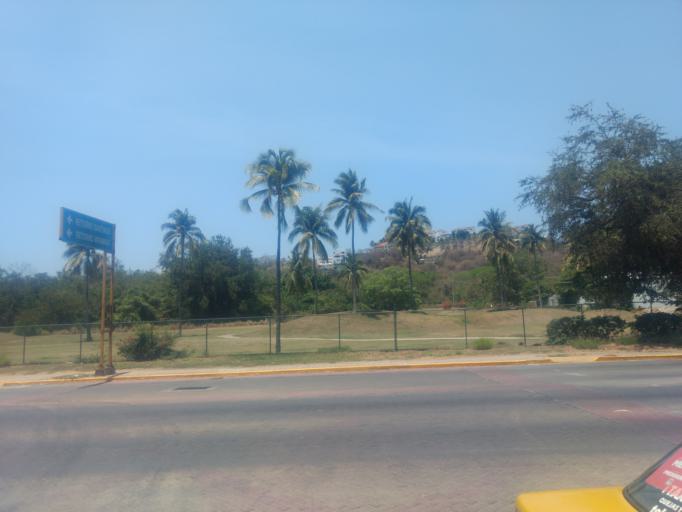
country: MX
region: Colima
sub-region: Manzanillo
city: Manzanillo
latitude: 19.1146
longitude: -104.3455
